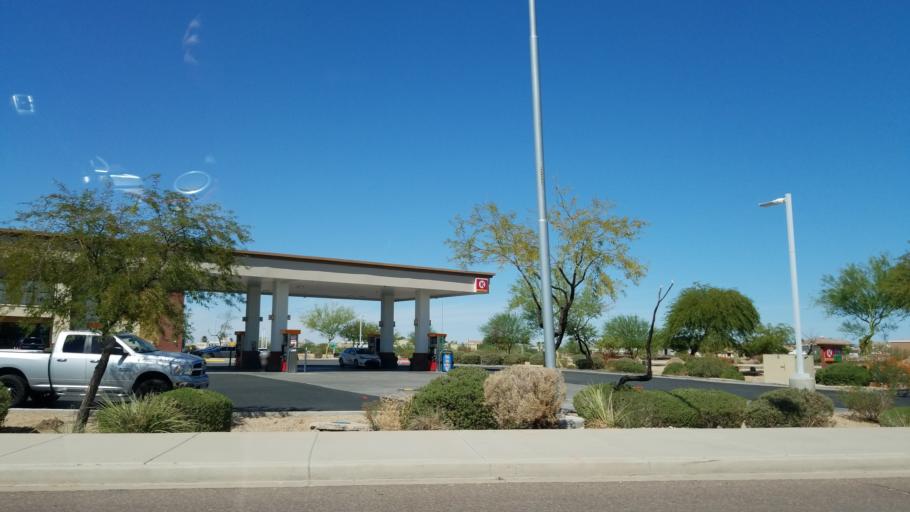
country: US
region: Arizona
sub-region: Maricopa County
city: Sun City West
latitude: 33.6958
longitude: -112.2757
